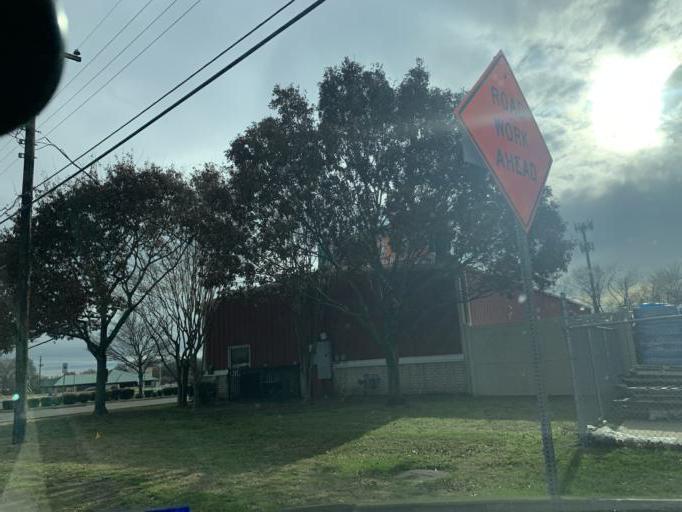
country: US
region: Texas
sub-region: Dallas County
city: Duncanville
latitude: 32.6355
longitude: -96.8989
